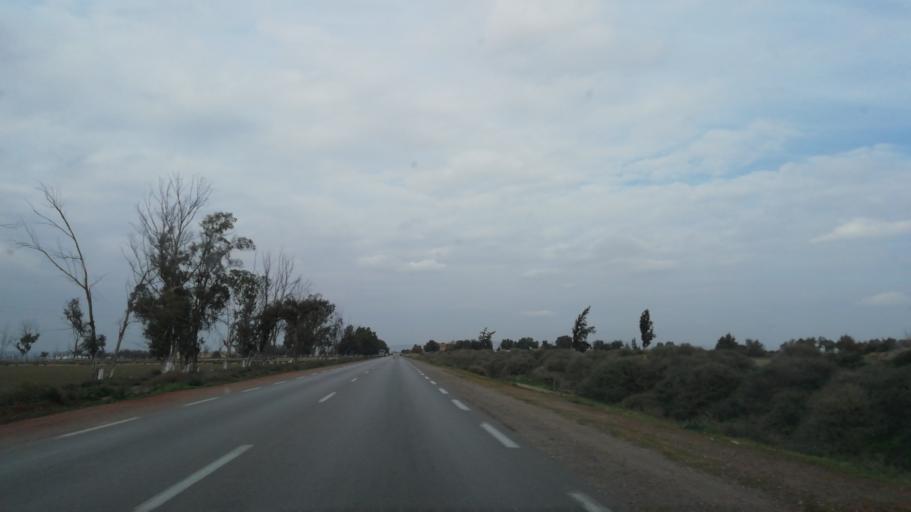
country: DZ
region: Mostaganem
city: Mostaganem
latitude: 35.6789
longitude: 0.0571
